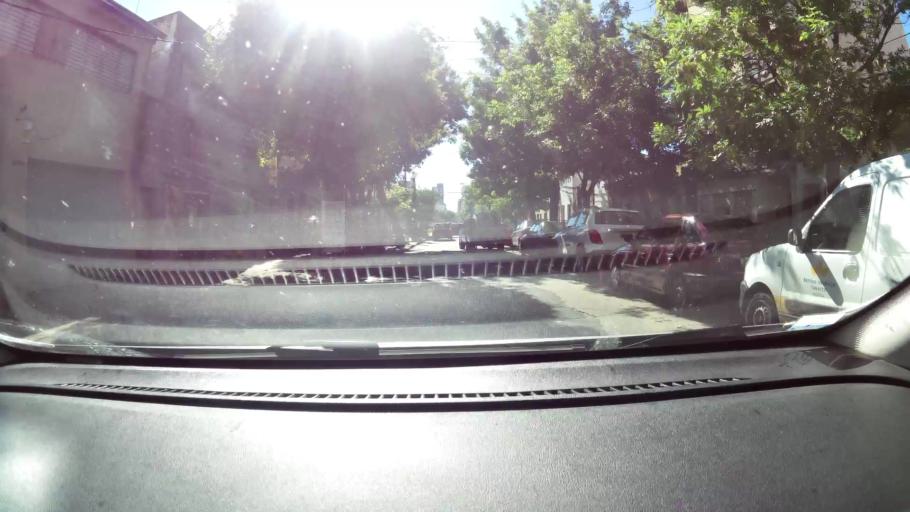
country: AR
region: Santa Fe
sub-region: Departamento de Rosario
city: Rosario
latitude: -32.9513
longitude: -60.6673
